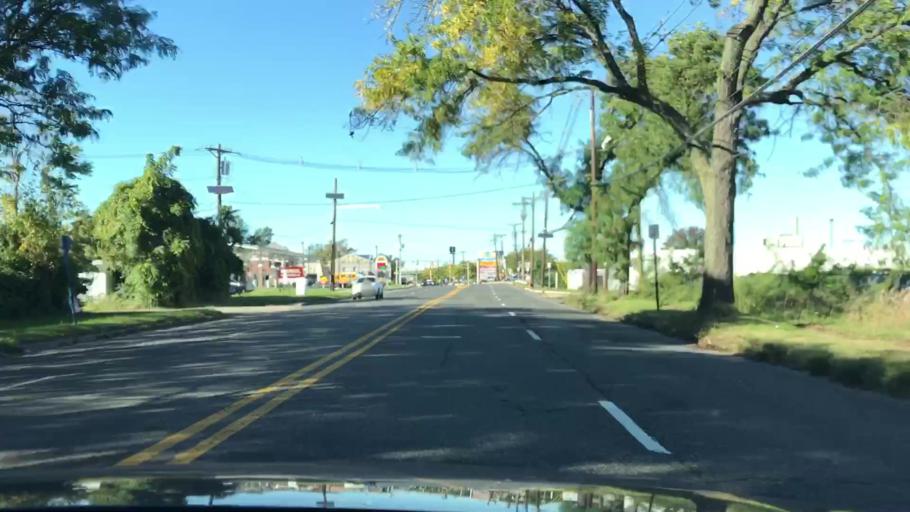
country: US
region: New Jersey
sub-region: Bergen County
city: Little Ferry
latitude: 40.8609
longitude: -74.0355
